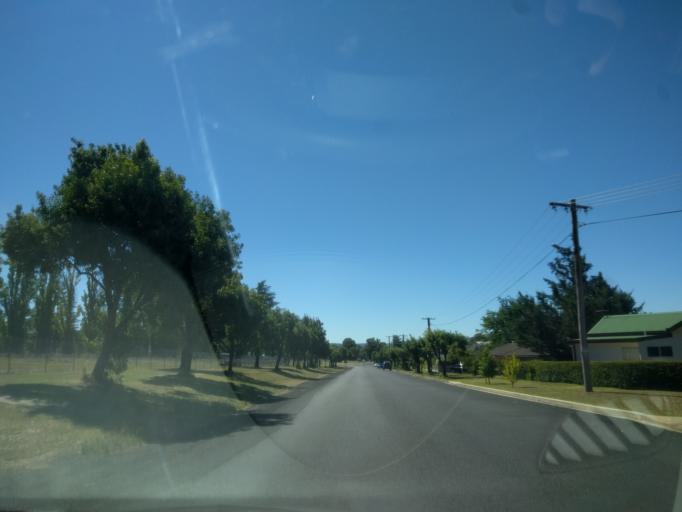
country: AU
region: New South Wales
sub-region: Armidale Dumaresq
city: Armidale
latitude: -30.5211
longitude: 151.6580
